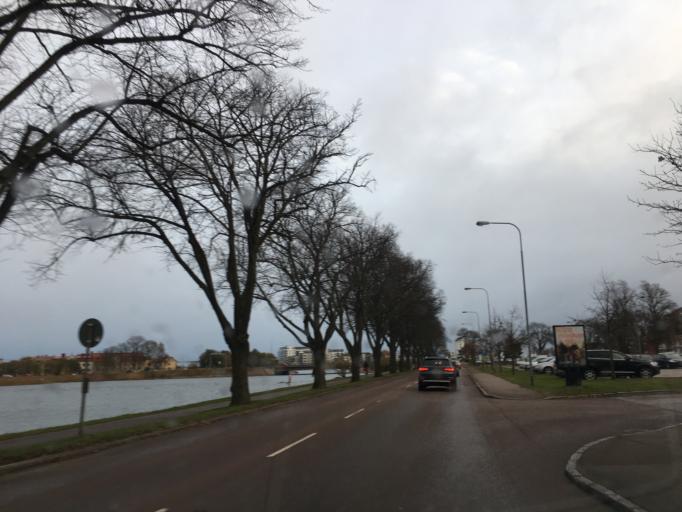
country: SE
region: Kalmar
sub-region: Kalmar Kommun
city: Kalmar
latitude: 56.6663
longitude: 16.3647
